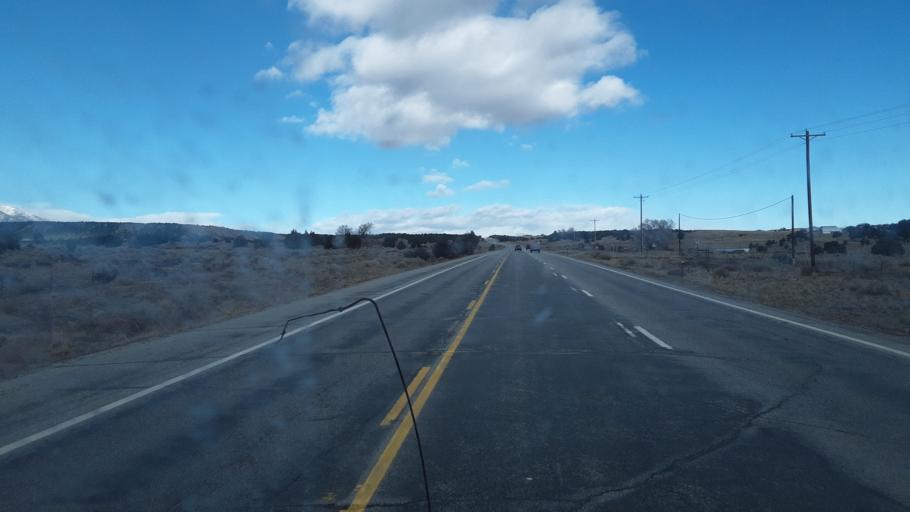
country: US
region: Colorado
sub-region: Chaffee County
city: Salida
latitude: 38.6454
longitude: -106.0838
